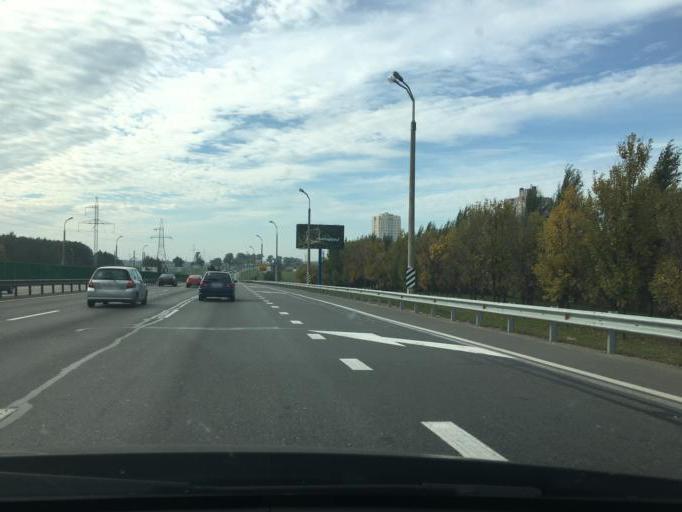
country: BY
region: Minsk
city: Shchomyslitsa
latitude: 53.8433
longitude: 27.4622
